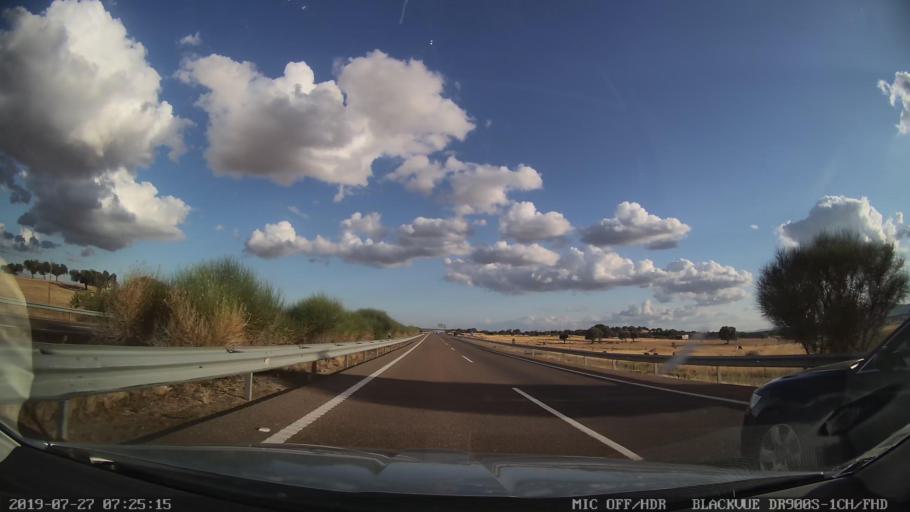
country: ES
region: Extremadura
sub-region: Provincia de Caceres
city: Puerto de Santa Cruz
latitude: 39.2805
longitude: -5.8560
